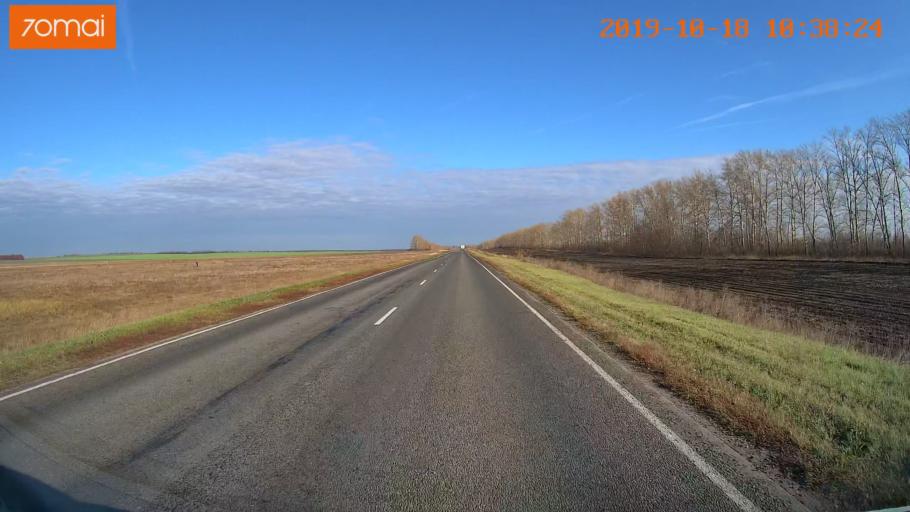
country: RU
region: Tula
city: Kurkino
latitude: 53.5725
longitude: 38.6411
